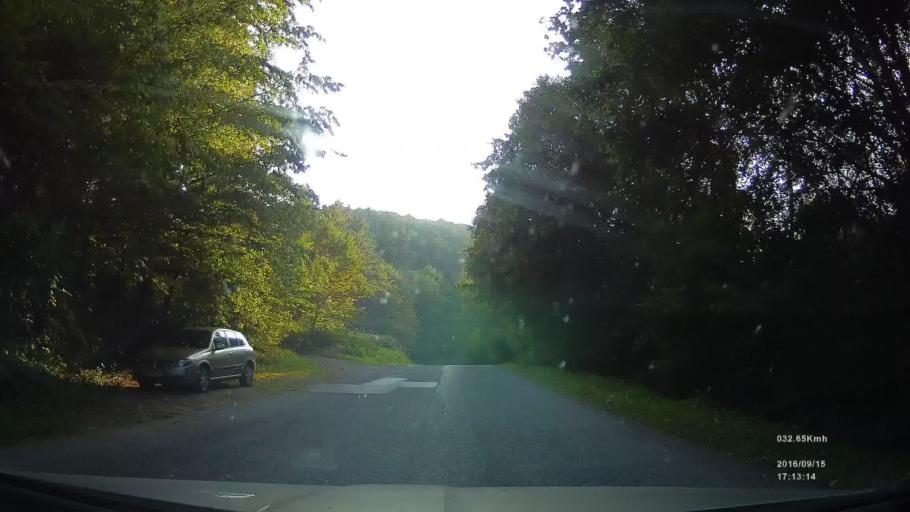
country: SK
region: Kosicky
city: Gelnica
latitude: 48.9099
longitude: 21.0938
